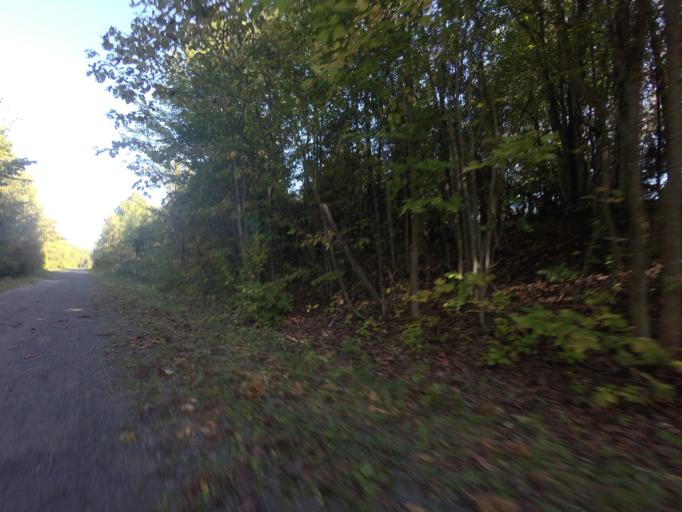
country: CA
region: Ontario
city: Hawkesbury
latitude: 45.5376
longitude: -74.6135
